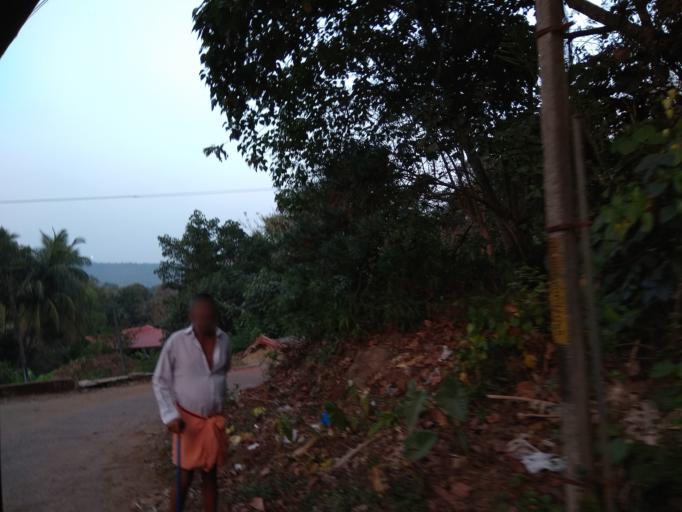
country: IN
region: Karnataka
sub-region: Dakshina Kannada
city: Mangalore
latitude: 12.9326
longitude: 74.8673
